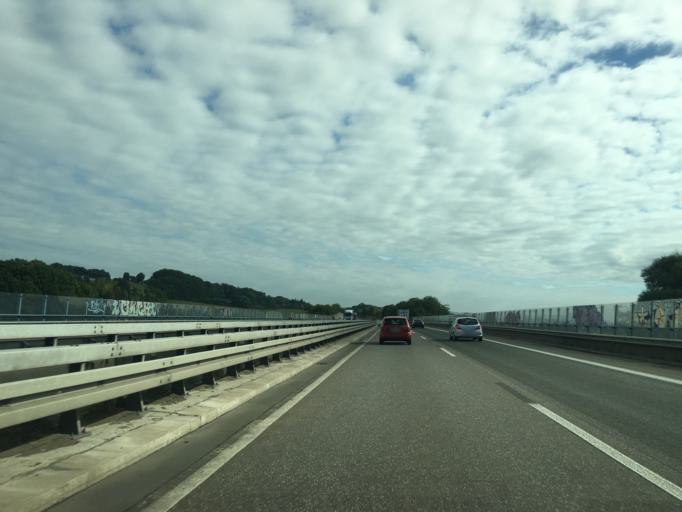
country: DE
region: North Rhine-Westphalia
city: Loehne
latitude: 52.1957
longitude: 8.6845
